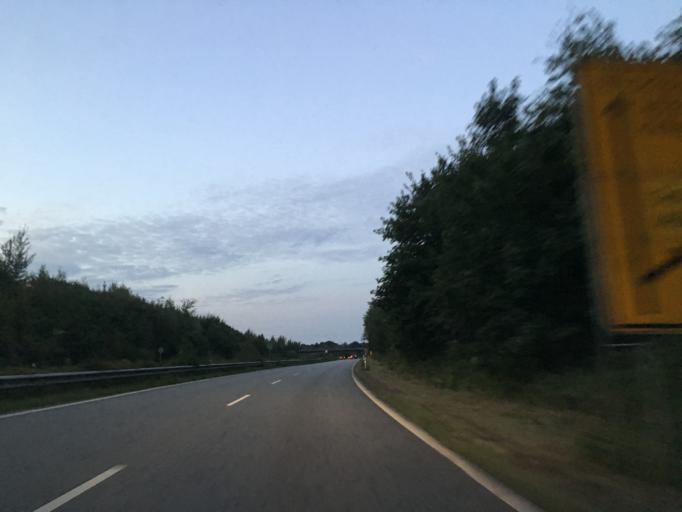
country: DE
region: Schleswig-Holstein
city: Monkeberg
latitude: 54.3382
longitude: 10.2057
